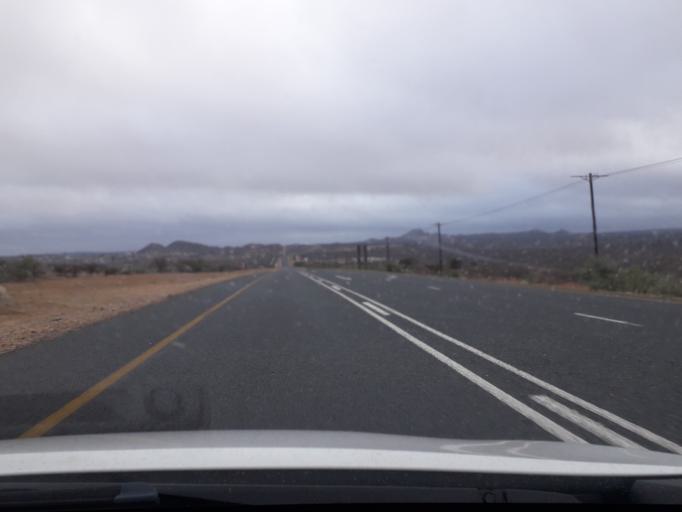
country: ZA
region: Limpopo
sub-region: Capricorn District Municipality
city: Dendron
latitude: -23.4637
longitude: 29.7348
